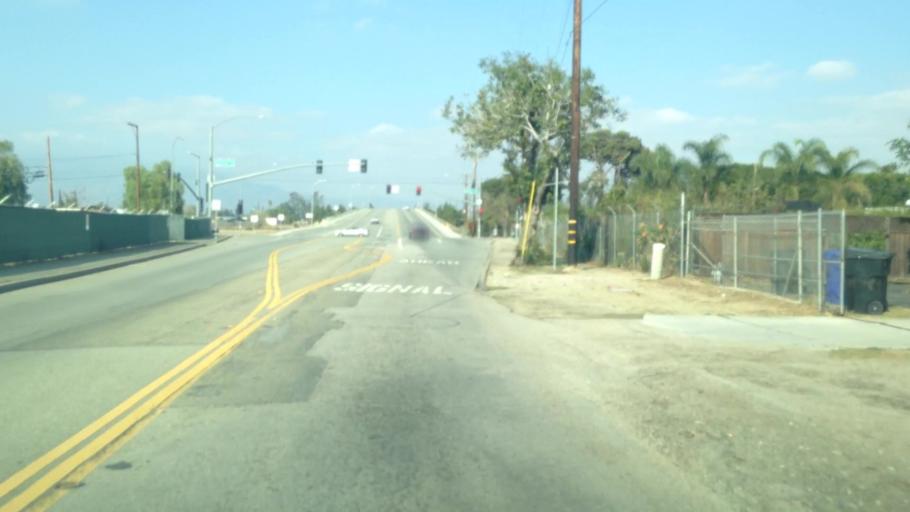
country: US
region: California
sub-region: San Bernardino County
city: Fontana
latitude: 34.0620
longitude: -117.4443
